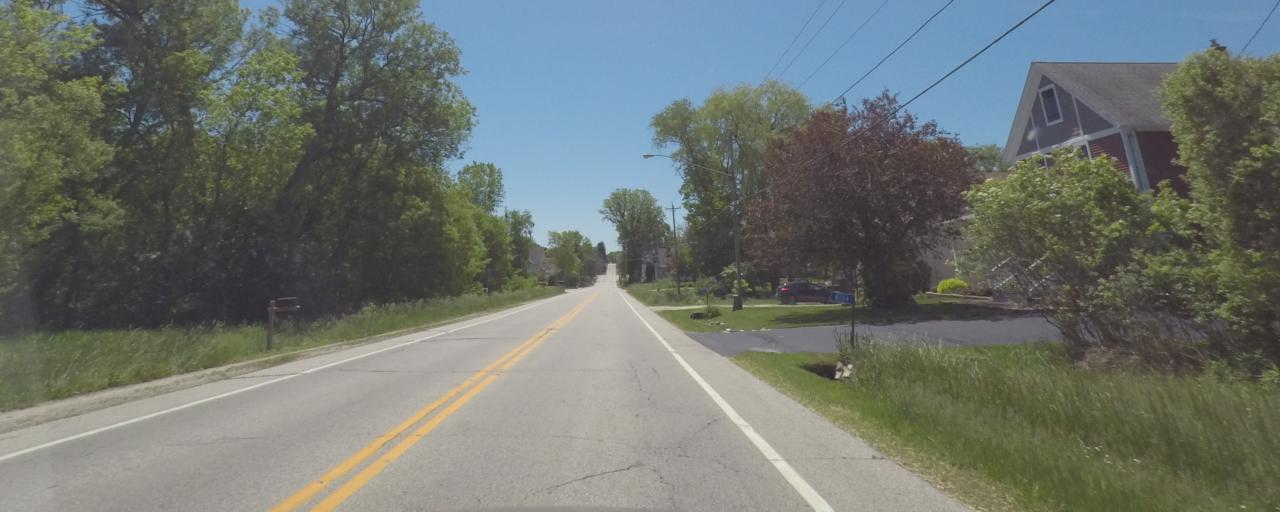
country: US
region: Wisconsin
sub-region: Sheboygan County
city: Random Lake
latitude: 43.5955
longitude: -88.0504
